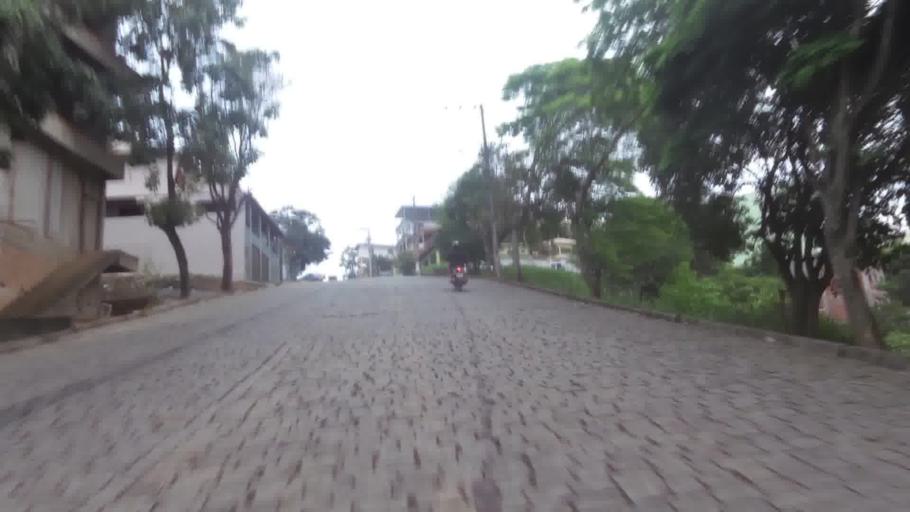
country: BR
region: Espirito Santo
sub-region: Iconha
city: Iconha
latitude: -20.7883
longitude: -40.8164
